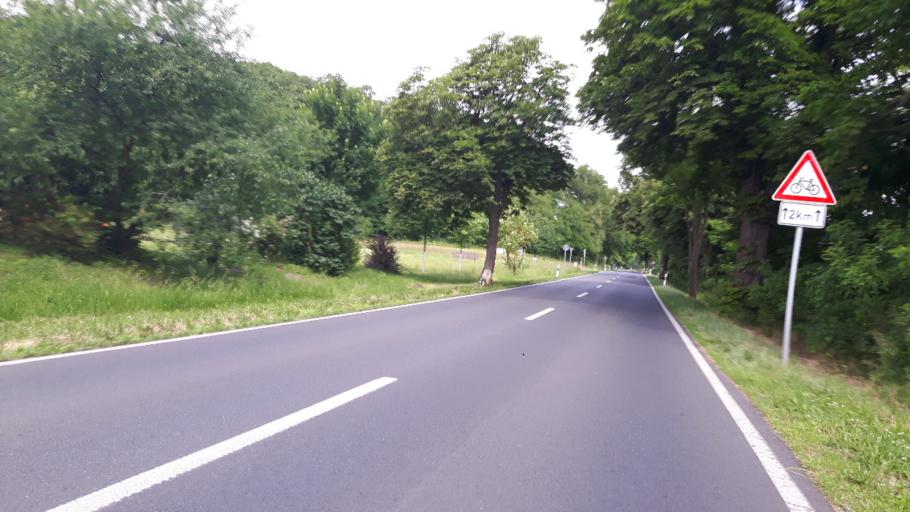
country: DE
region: Brandenburg
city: Mescherin
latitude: 53.2593
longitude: 14.4361
